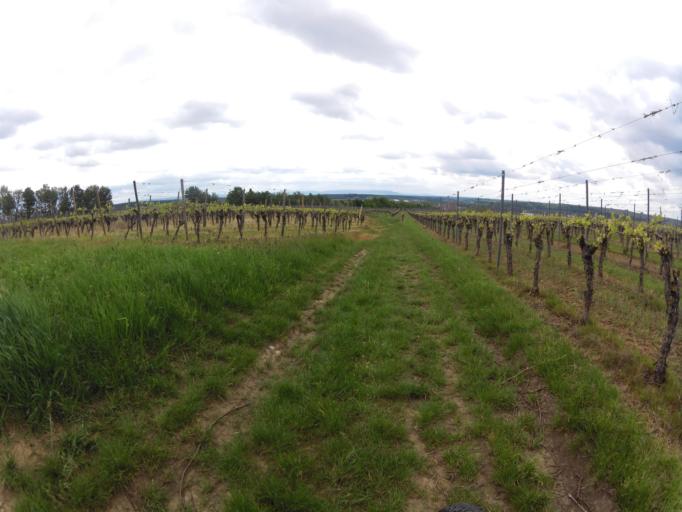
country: DE
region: Bavaria
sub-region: Regierungsbezirk Unterfranken
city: Volkach
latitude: 49.8780
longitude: 10.2263
